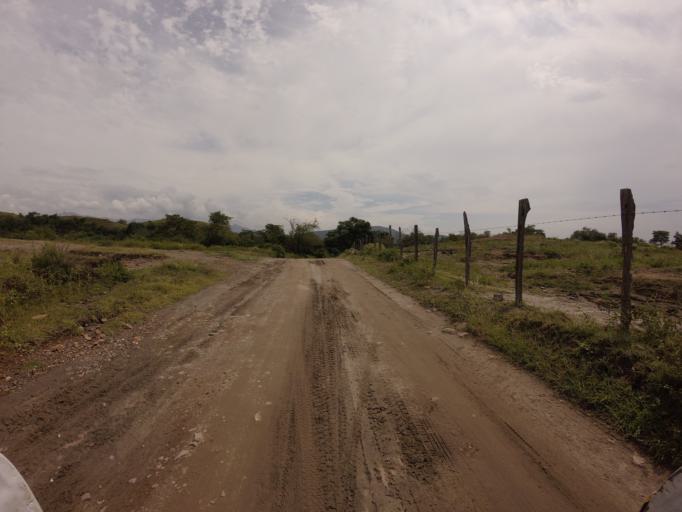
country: CO
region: Tolima
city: Natagaima
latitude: 3.4526
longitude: -75.1437
